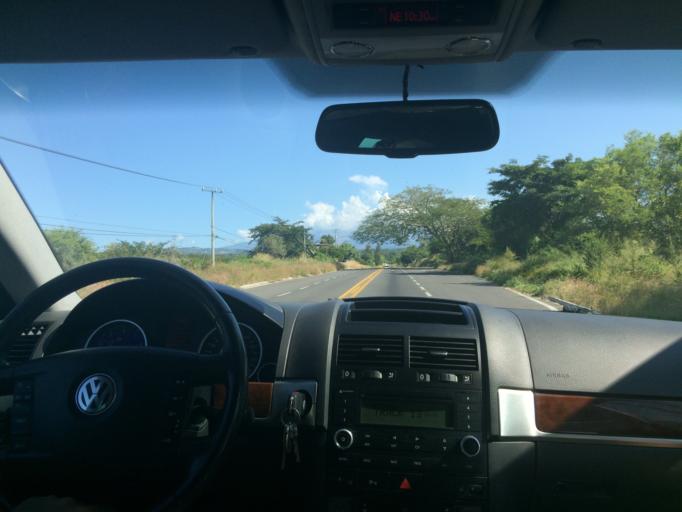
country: MX
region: Colima
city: Comala
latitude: 19.3427
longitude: -103.7421
